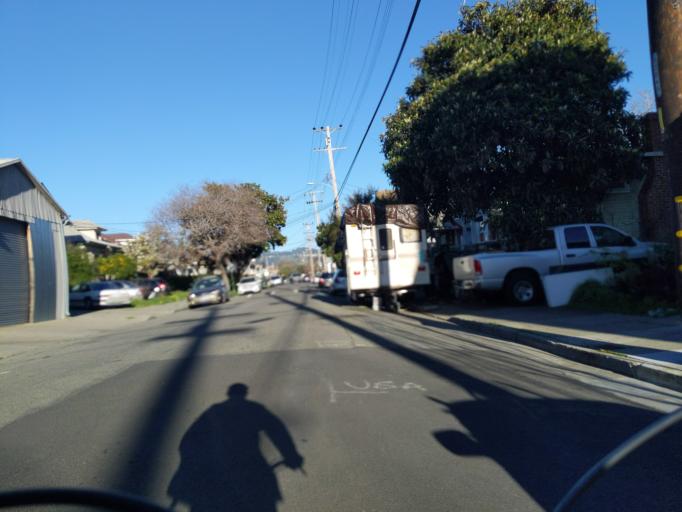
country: US
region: California
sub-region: Alameda County
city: Emeryville
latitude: 37.8399
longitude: -122.2762
